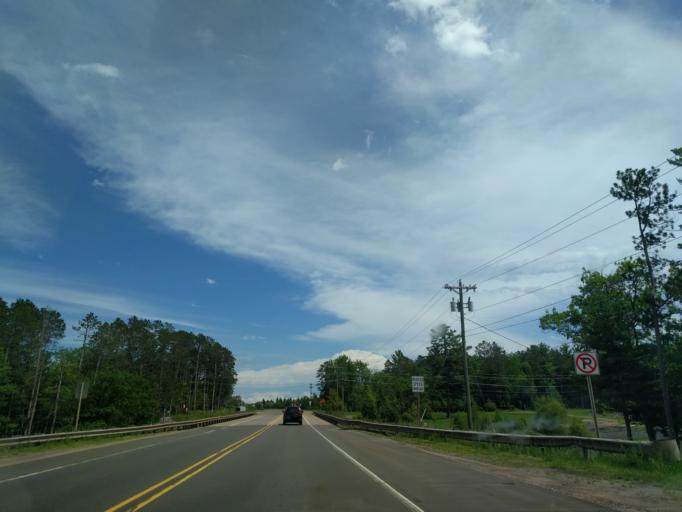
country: US
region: Michigan
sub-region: Marquette County
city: Trowbridge Park
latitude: 46.5723
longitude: -87.4111
